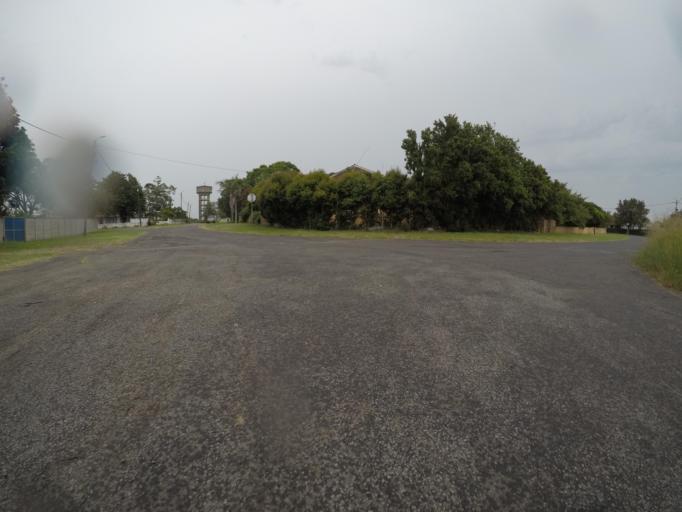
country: ZA
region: Eastern Cape
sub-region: Buffalo City Metropolitan Municipality
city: East London
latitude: -32.9688
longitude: 27.8300
